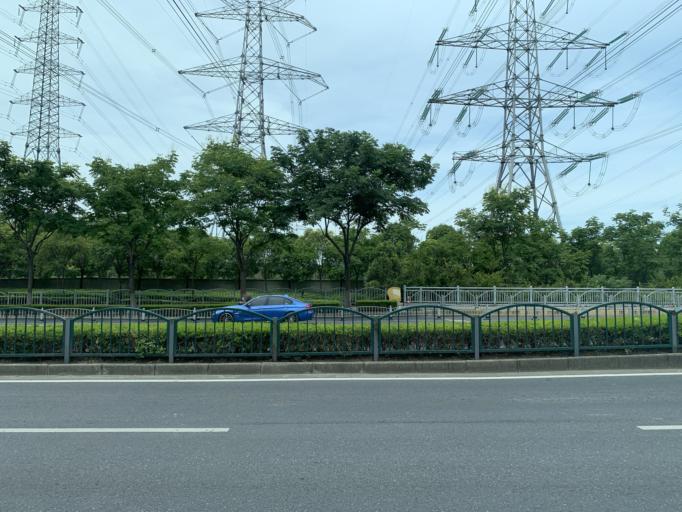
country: CN
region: Shanghai Shi
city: Kangqiao
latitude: 31.1639
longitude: 121.5594
